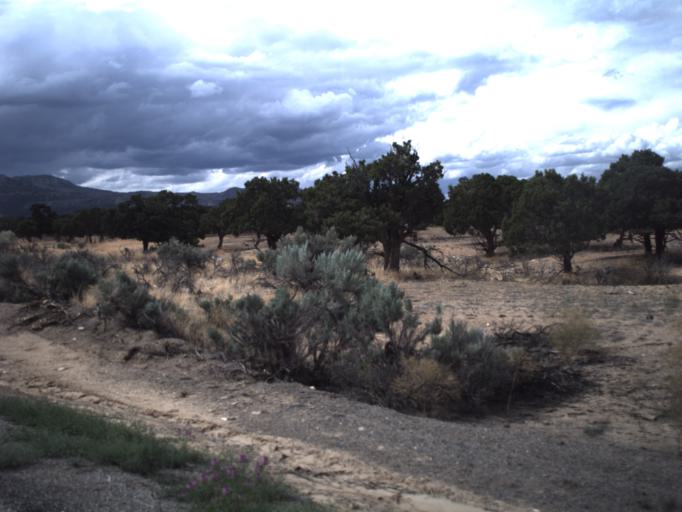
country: US
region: Utah
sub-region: Emery County
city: Huntington
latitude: 39.4845
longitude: -110.9270
